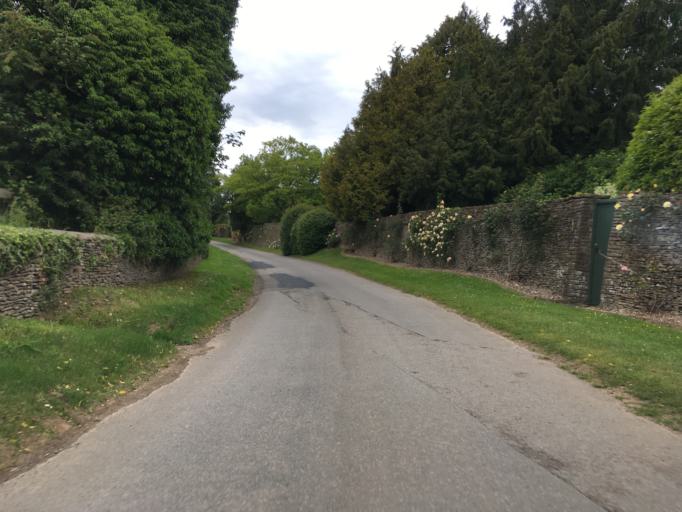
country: GB
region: England
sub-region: Wiltshire
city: Luckington
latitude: 51.5963
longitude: -2.2131
